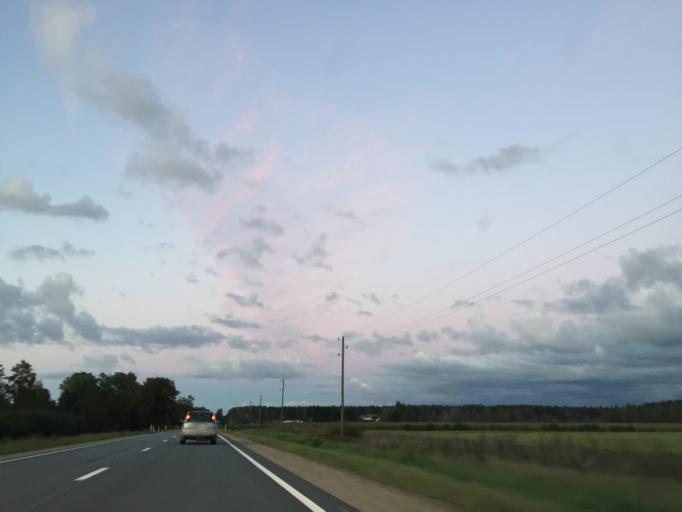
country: LV
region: Jurmala
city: Jurmala
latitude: 56.9062
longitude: 23.7671
